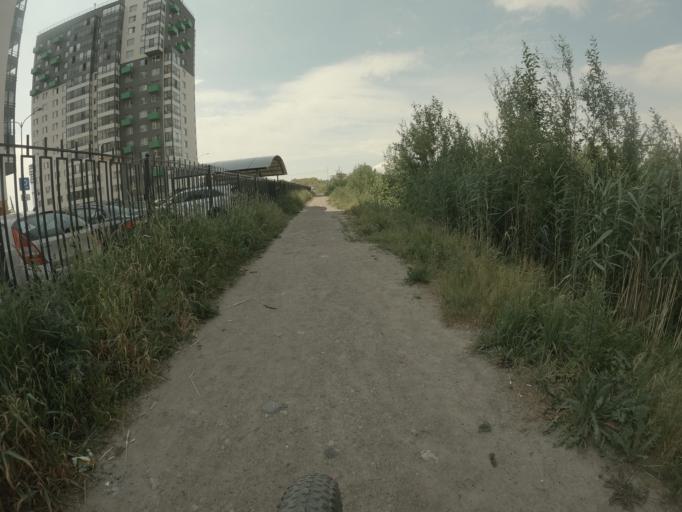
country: RU
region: St.-Petersburg
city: Krasnogvargeisky
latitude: 59.9205
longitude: 30.4371
